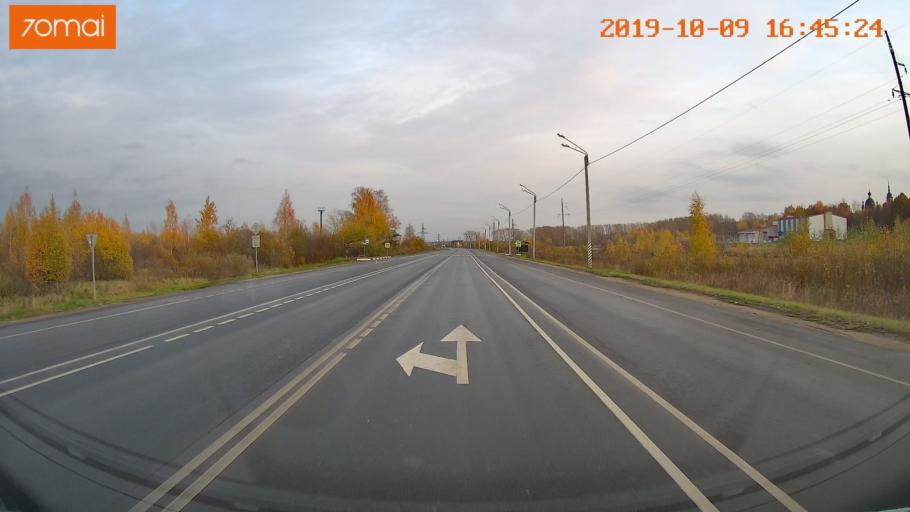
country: RU
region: Kostroma
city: Volgorechensk
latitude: 57.4466
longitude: 41.1543
